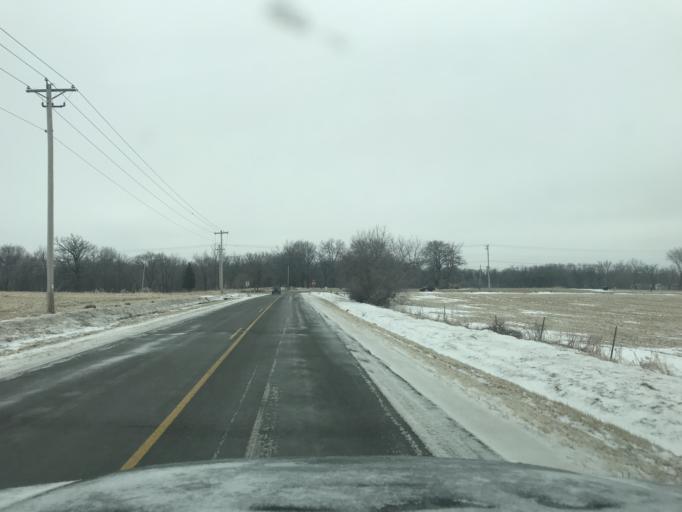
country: US
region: Wisconsin
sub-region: Dane County
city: Cottage Grove
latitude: 43.0911
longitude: -89.2295
